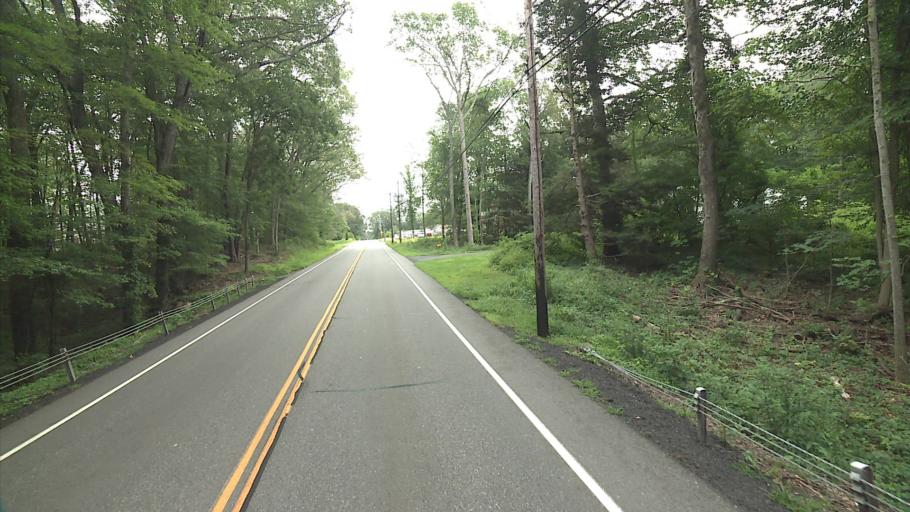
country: US
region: Connecticut
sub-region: Tolland County
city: Storrs
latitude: 41.8653
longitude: -72.1949
